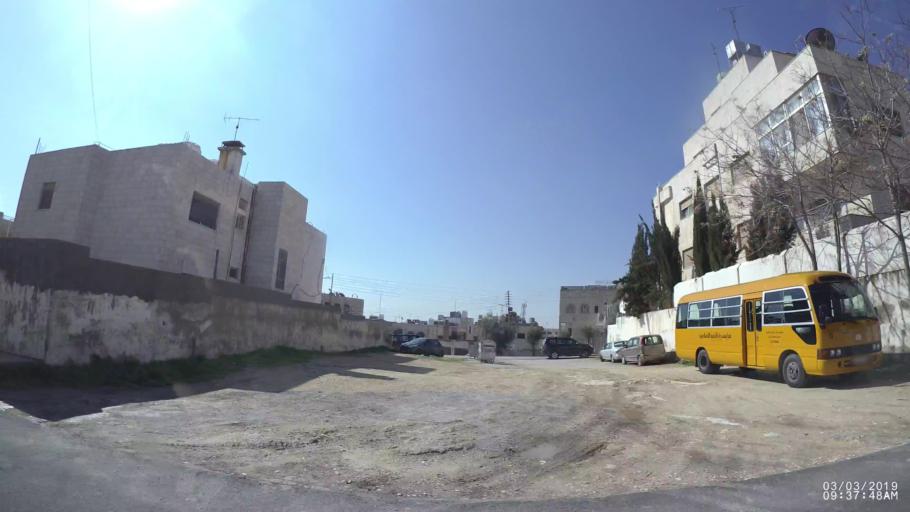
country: JO
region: Amman
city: Al Jubayhah
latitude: 32.0001
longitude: 35.8930
